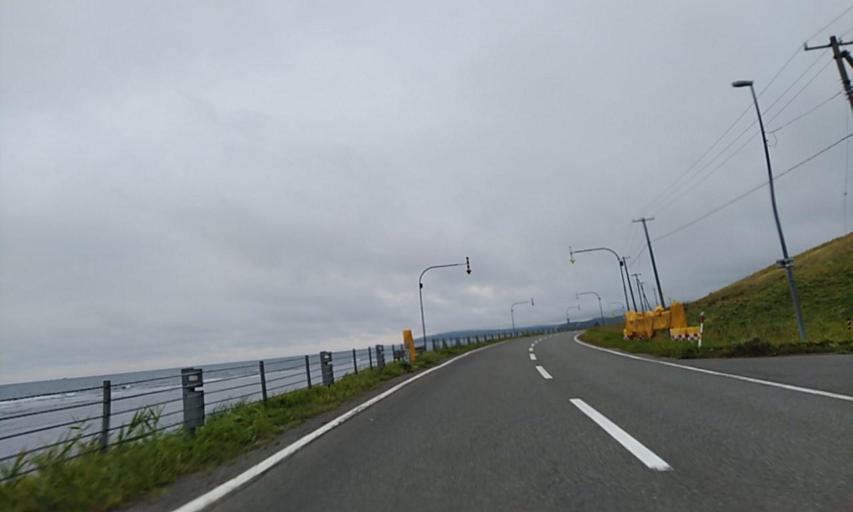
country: JP
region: Hokkaido
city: Makubetsu
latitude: 45.5073
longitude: 141.9626
